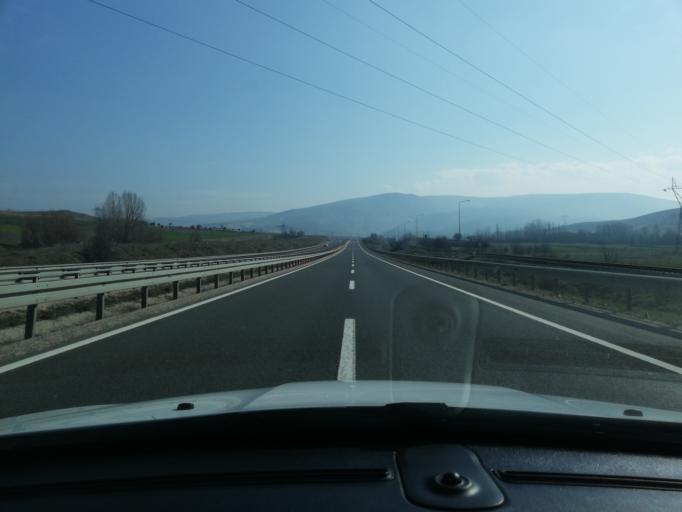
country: TR
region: Cankiri
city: Cerkes
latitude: 40.8376
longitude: 32.7477
